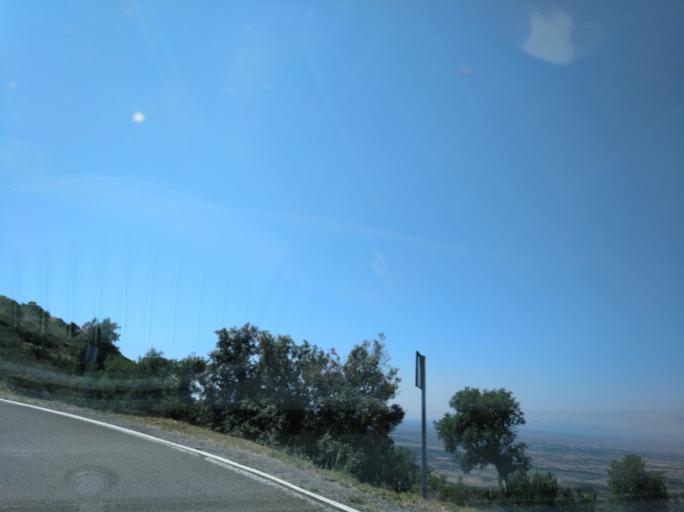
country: ES
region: Catalonia
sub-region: Provincia de Girona
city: Pau
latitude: 42.3314
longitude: 3.1301
